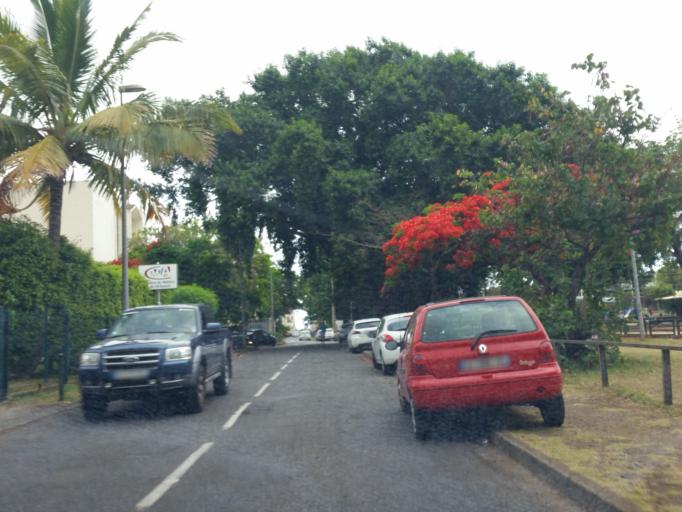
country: RE
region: Reunion
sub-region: Reunion
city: Saint-Denis
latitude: -20.8898
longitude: 55.4660
